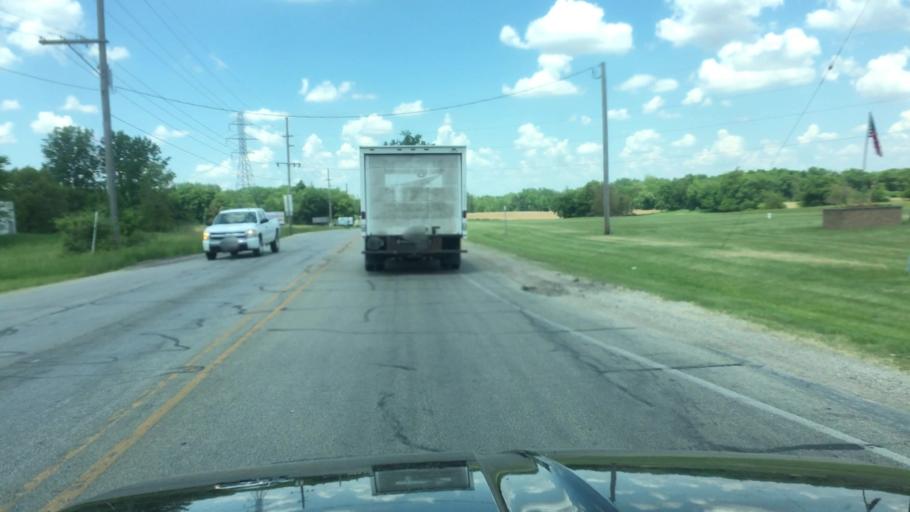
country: US
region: Indiana
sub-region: Kosciusko County
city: North Webster
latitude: 41.3090
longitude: -85.6910
